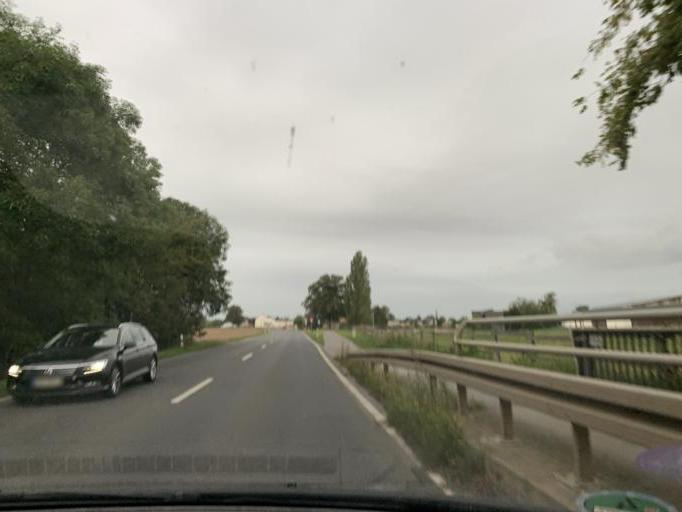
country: DE
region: North Rhine-Westphalia
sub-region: Regierungsbezirk Koln
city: Niederzier
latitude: 50.8378
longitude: 6.4314
